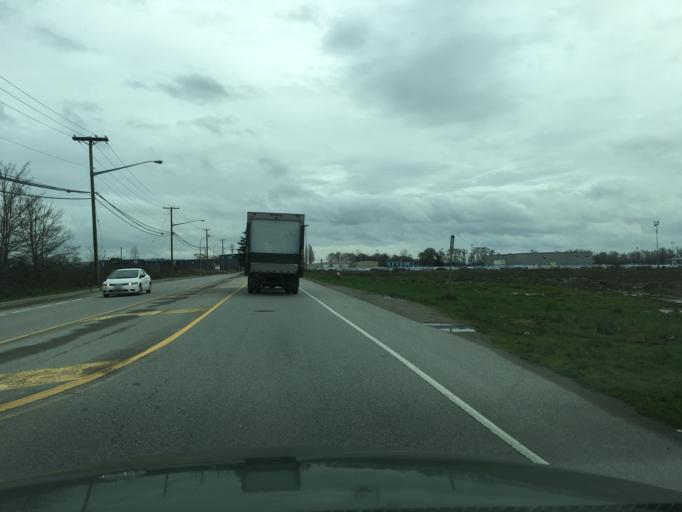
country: CA
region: British Columbia
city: Ladner
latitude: 49.1335
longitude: -123.0752
